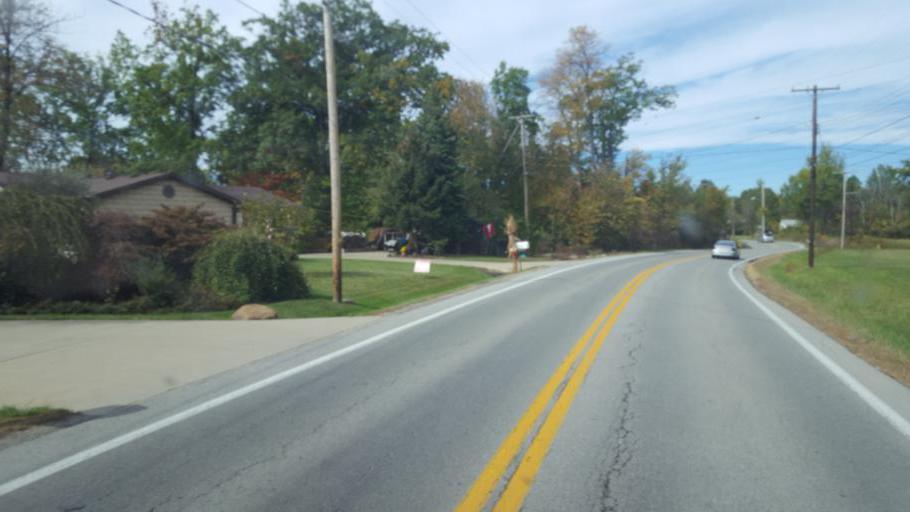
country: US
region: Ohio
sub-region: Lorain County
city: Amherst
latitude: 41.4231
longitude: -82.2267
